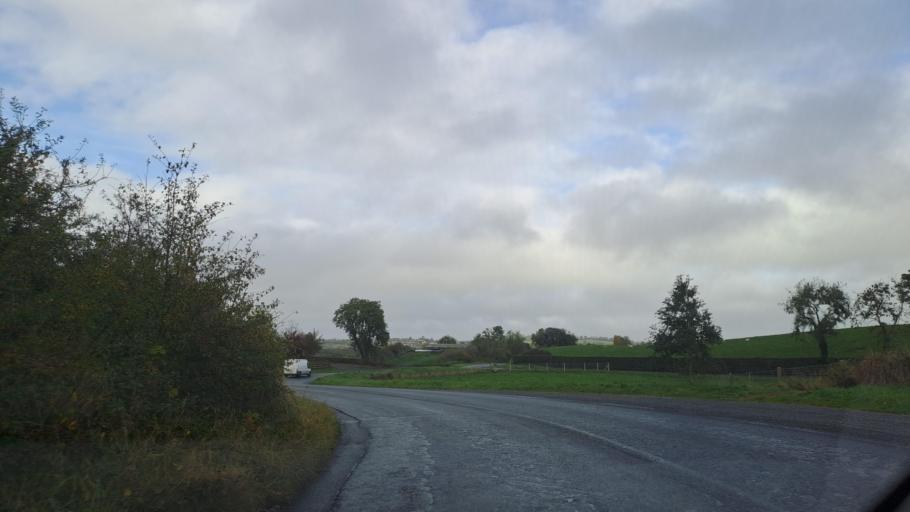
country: IE
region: Ulster
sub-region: County Monaghan
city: Carrickmacross
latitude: 53.9532
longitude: -6.7150
